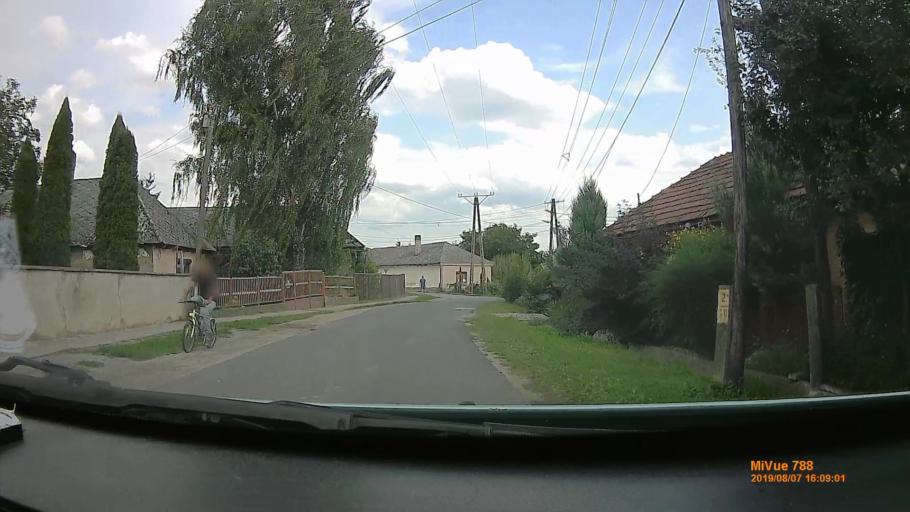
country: HU
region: Borsod-Abauj-Zemplen
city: Gonc
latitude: 48.5007
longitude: 21.2282
